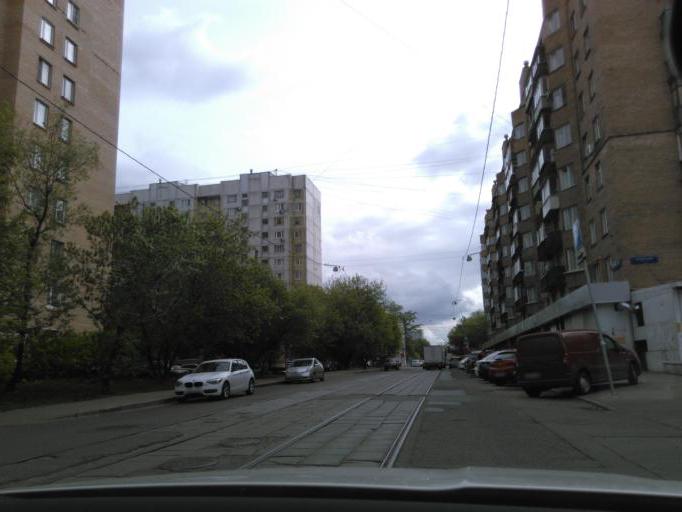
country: RU
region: Moscow
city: Mar'ina Roshcha
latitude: 55.7883
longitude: 37.6113
